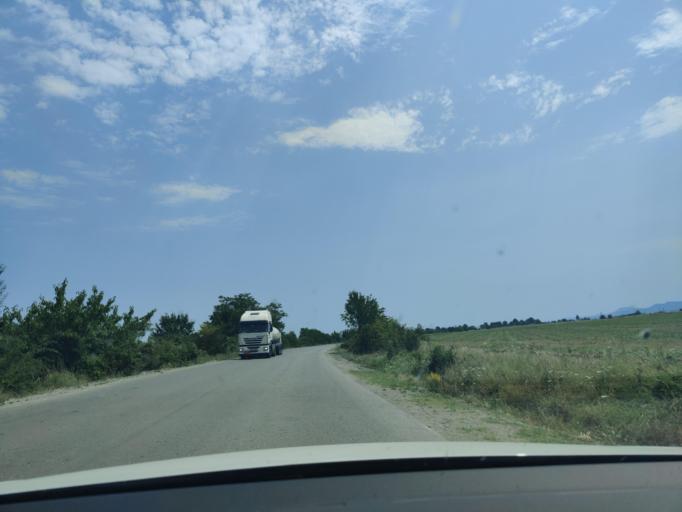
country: BG
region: Vidin
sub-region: Obshtina Ruzhintsi
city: Ruzhintsi
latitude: 43.5578
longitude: 22.9334
